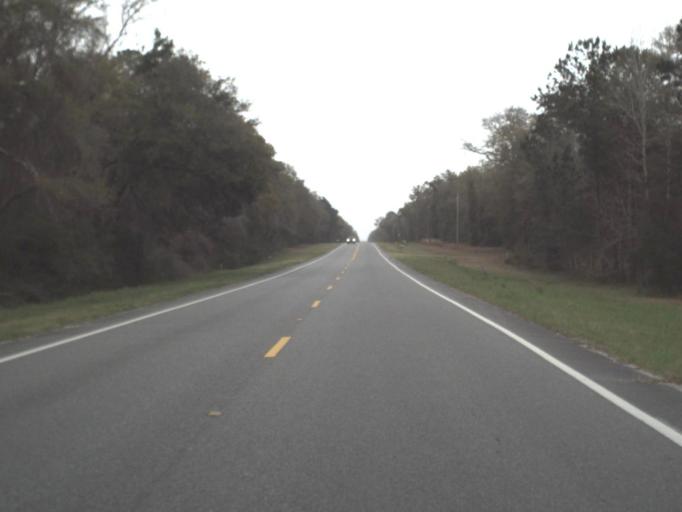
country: US
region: Florida
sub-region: Wakulla County
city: Crawfordville
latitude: 30.1438
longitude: -84.3024
